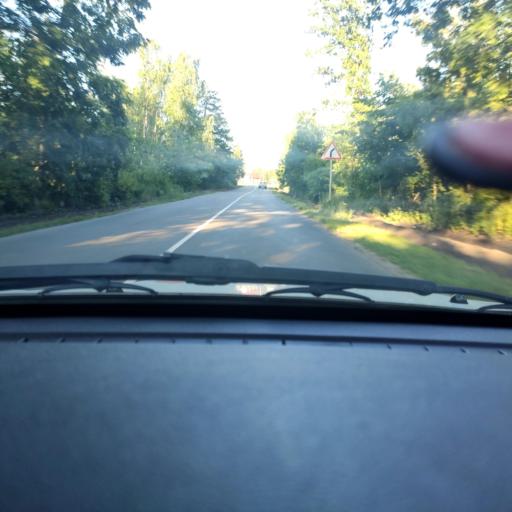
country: RU
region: Voronezj
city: Ramon'
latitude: 51.8924
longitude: 39.2394
